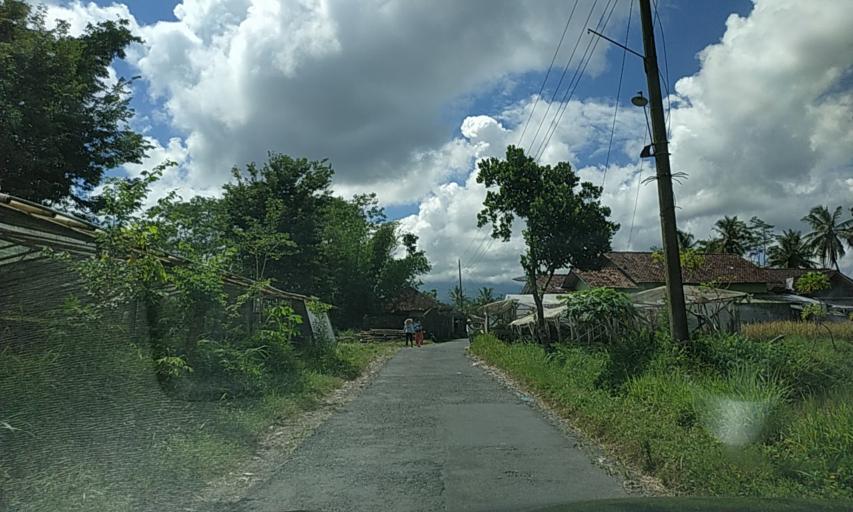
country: ID
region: Central Java
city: Muntilan
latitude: -7.5415
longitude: 110.3383
